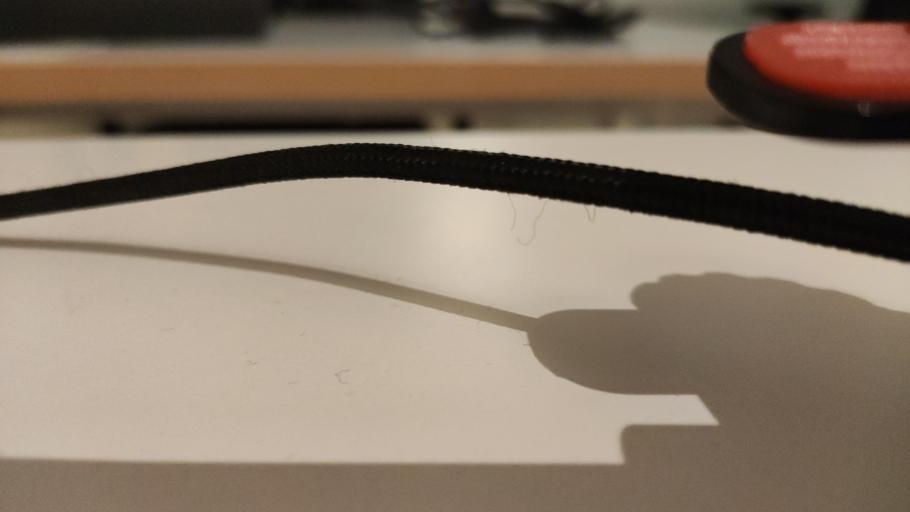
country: RU
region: Moskovskaya
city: Kurovskoye
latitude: 55.6033
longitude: 38.9265
